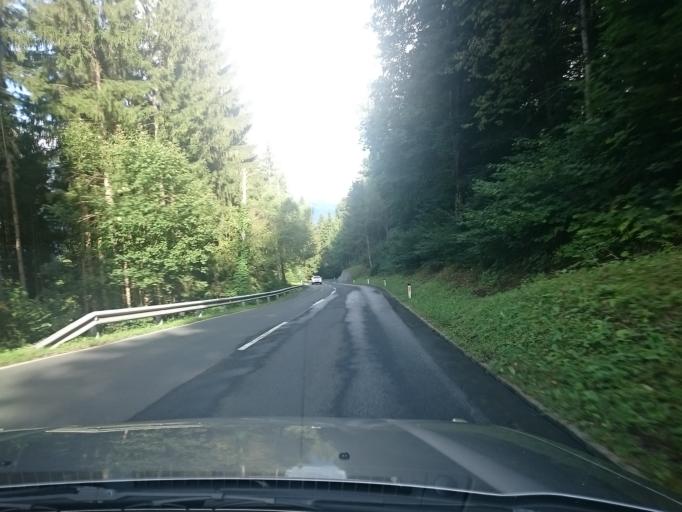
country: AT
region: Carinthia
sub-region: Politischer Bezirk Spittal an der Drau
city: Oberdrauburg
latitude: 46.6625
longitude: 12.9934
